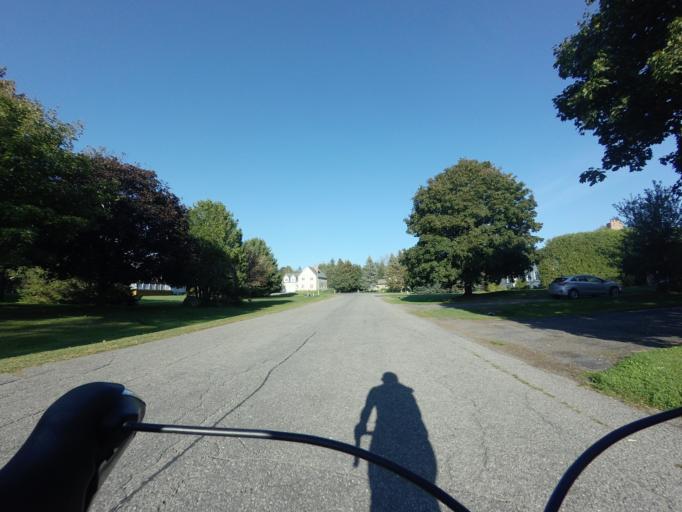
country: CA
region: Ontario
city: Bells Corners
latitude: 45.2223
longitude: -75.6917
